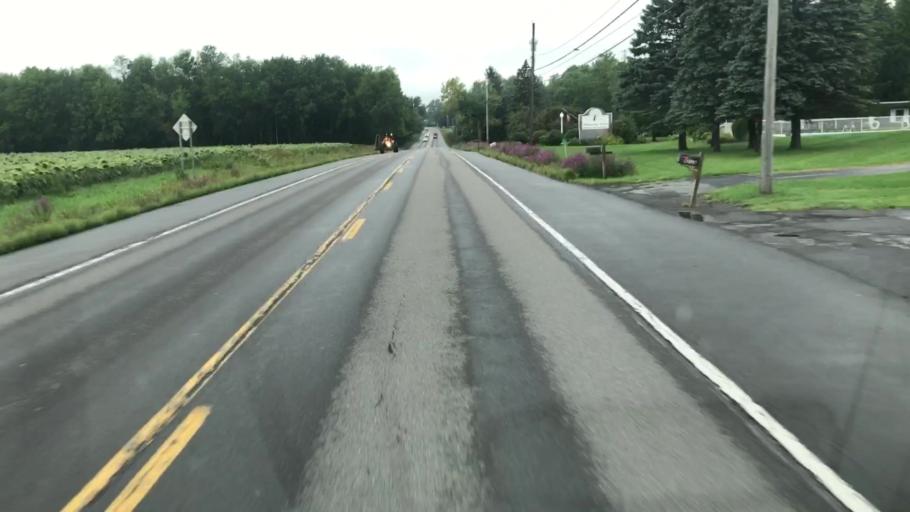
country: US
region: New York
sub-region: Onondaga County
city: Skaneateles
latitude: 42.9433
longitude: -76.4611
